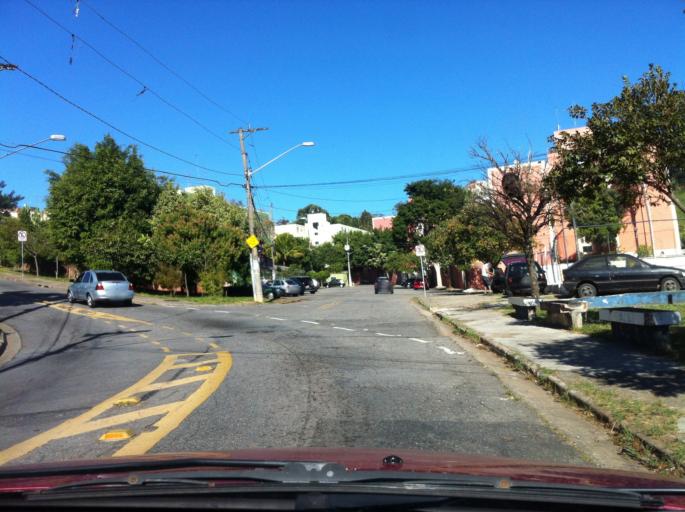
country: BR
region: Sao Paulo
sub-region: Ferraz De Vasconcelos
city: Ferraz de Vasconcelos
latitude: -23.5465
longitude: -46.4427
